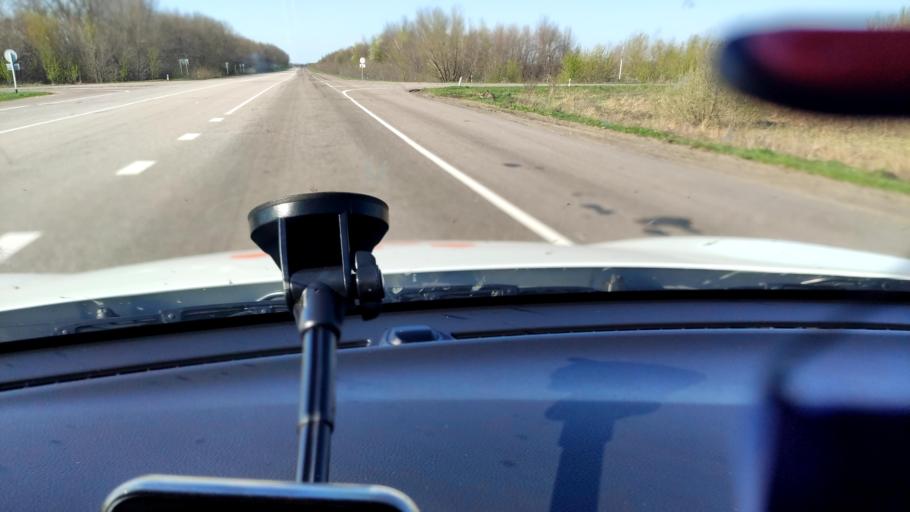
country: RU
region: Voronezj
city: Kolodeznyy
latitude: 51.2931
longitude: 39.0402
